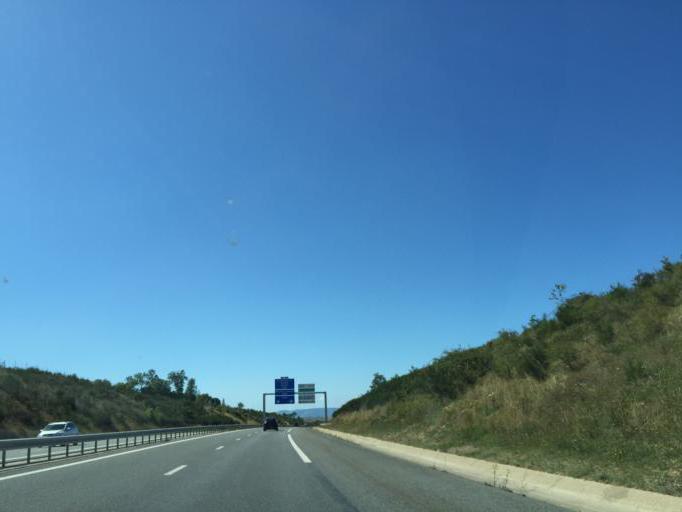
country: FR
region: Midi-Pyrenees
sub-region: Departement de l'Aveyron
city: La Cavalerie
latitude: 44.0004
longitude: 3.1577
